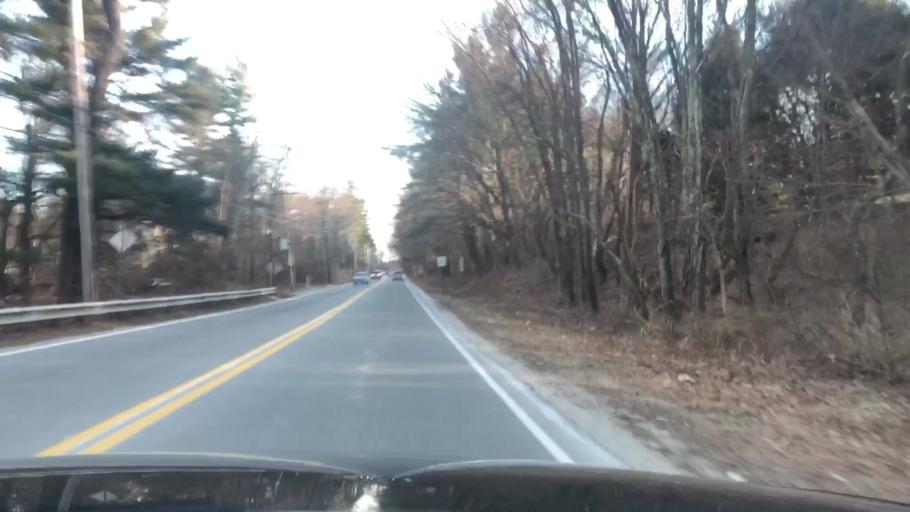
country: US
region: Massachusetts
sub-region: Worcester County
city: Bolton
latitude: 42.4450
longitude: -71.6244
